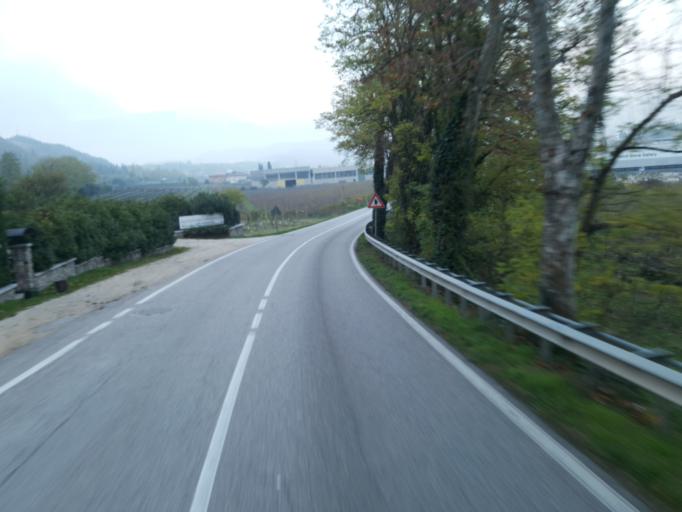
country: IT
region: Veneto
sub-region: Provincia di Verona
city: Pastrengo
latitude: 45.5121
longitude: 10.7976
